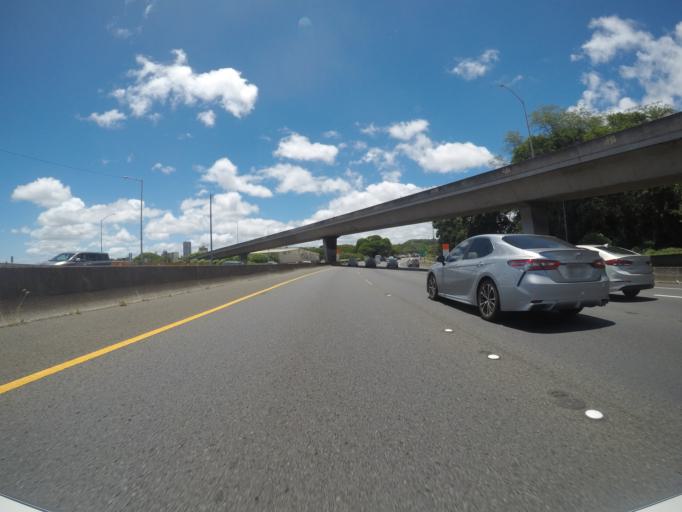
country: US
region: Hawaii
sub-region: Honolulu County
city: Halawa Heights
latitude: 21.3439
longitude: -157.8920
